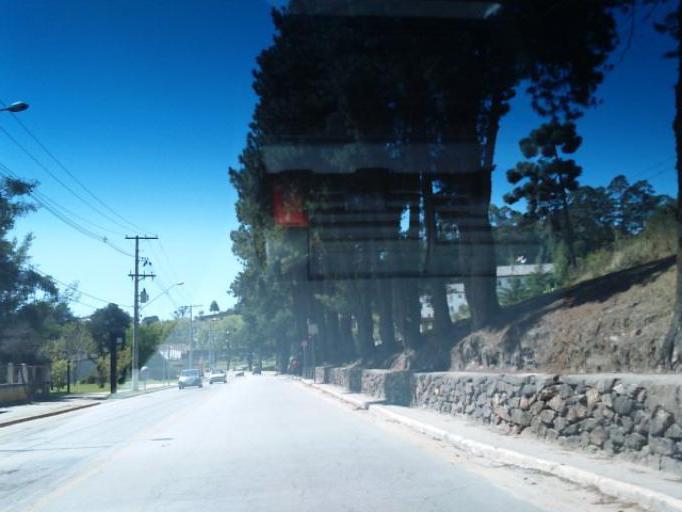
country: BR
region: Sao Paulo
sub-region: Campos Do Jordao
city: Campos do Jordao
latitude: -22.7513
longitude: -45.6079
